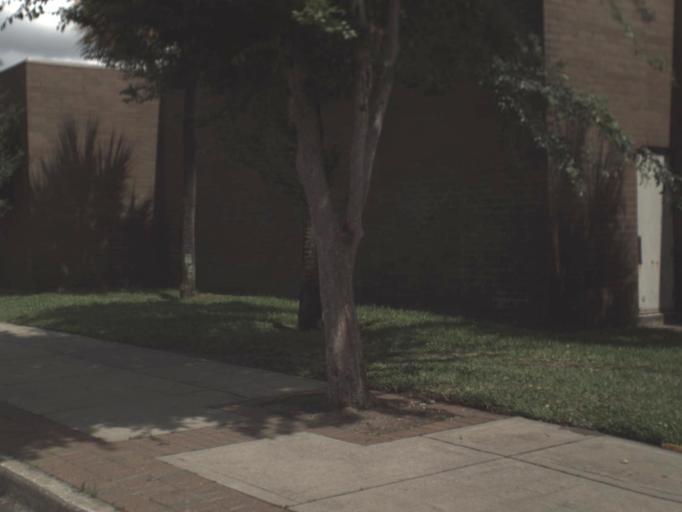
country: US
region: Florida
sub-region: Duval County
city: Jacksonville
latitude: 30.3331
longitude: -81.6562
